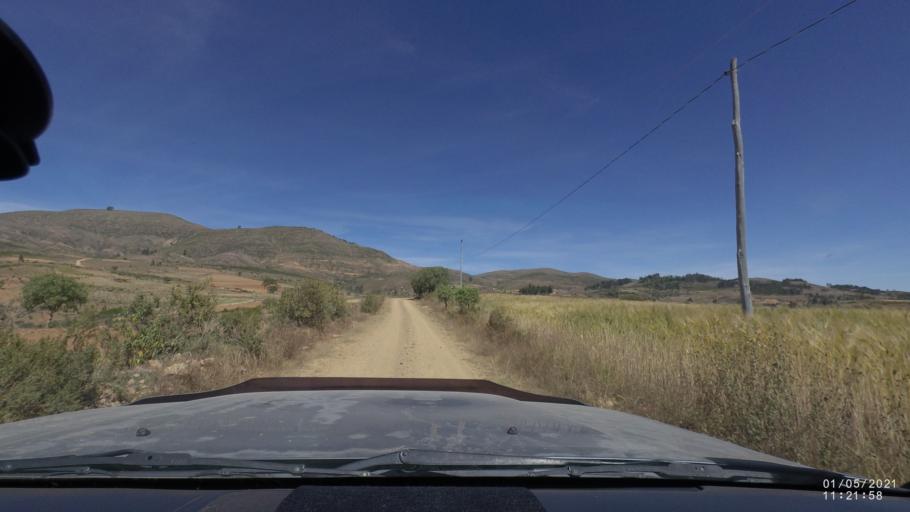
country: BO
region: Cochabamba
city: Tarata
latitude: -17.6474
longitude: -66.1294
